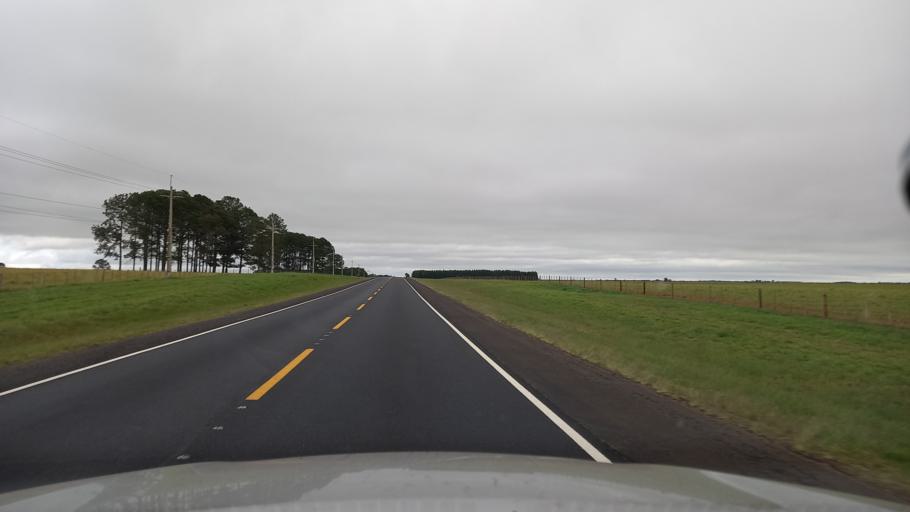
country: PY
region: Misiones
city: San Patricio
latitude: -26.9991
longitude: -56.7581
